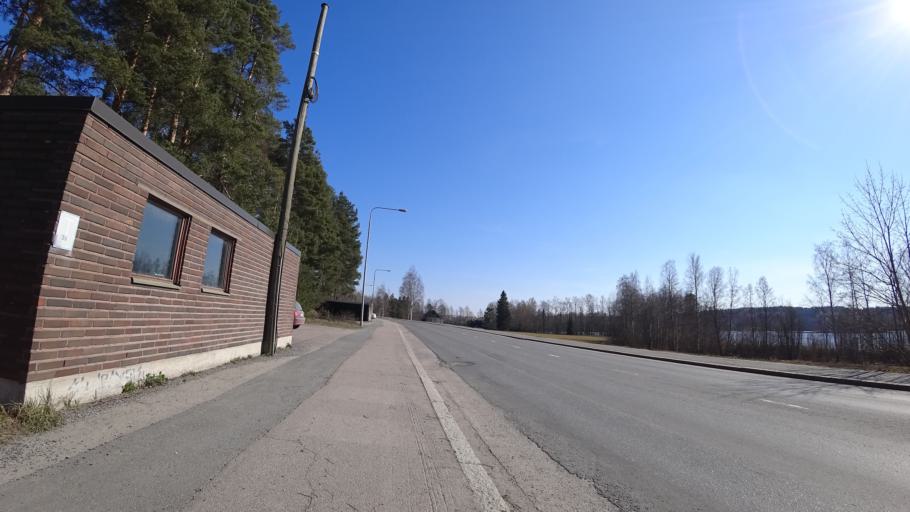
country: FI
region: Pirkanmaa
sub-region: Tampere
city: Pirkkala
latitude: 61.5159
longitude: 23.6504
